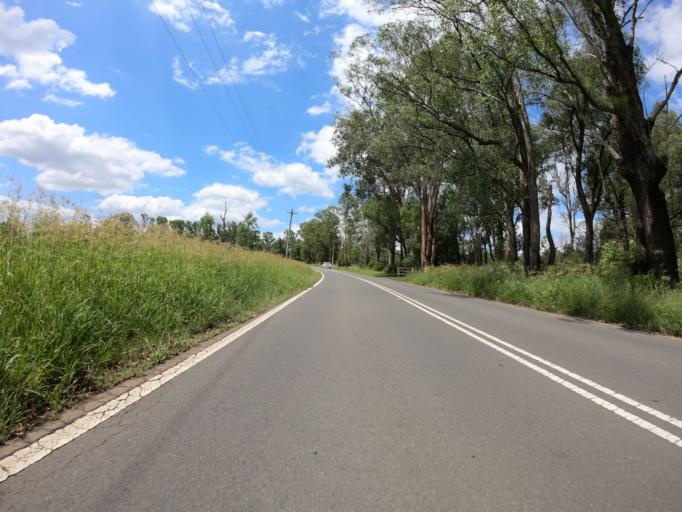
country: AU
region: New South Wales
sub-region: Penrith Municipality
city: Mulgoa
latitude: -33.8297
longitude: 150.6628
